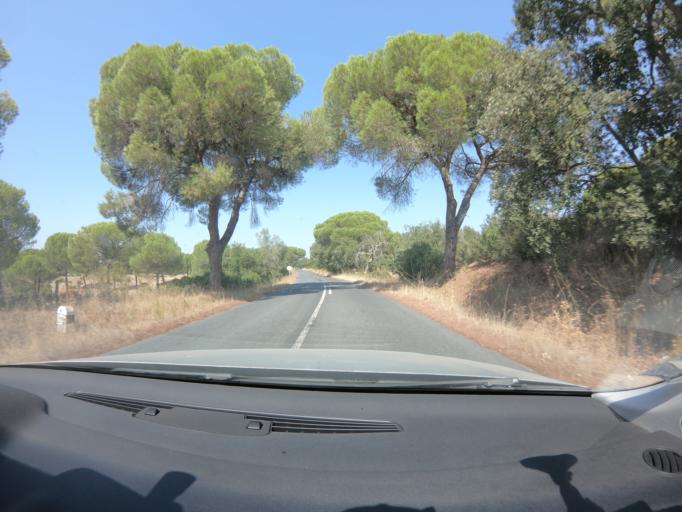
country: PT
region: Setubal
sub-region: Alcacer do Sal
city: Alcacer do Sal
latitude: 38.3010
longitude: -8.4049
